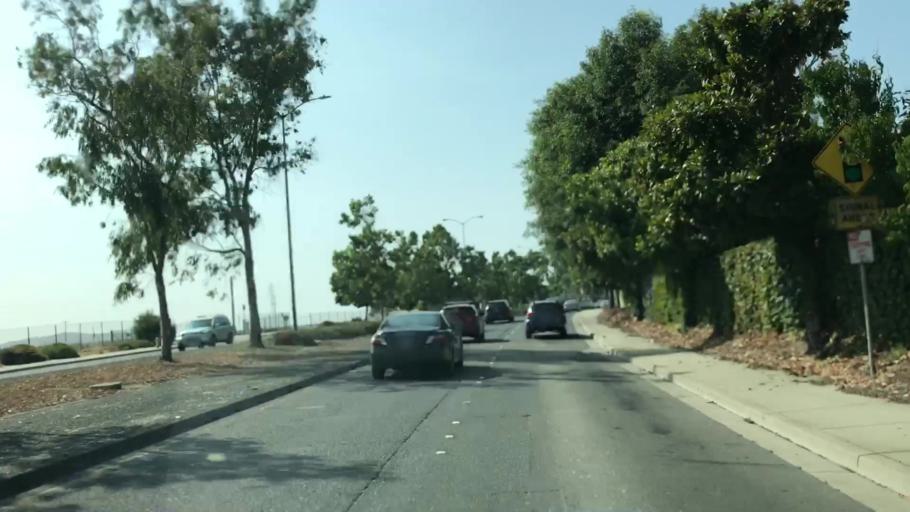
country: US
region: California
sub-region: Alameda County
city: Newark
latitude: 37.5696
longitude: -122.0752
